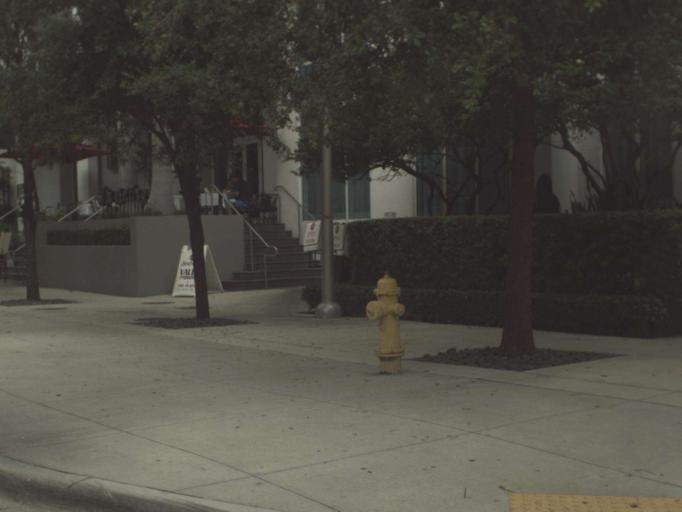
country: US
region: Florida
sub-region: Miami-Dade County
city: Miami
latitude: 25.7645
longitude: -80.1910
